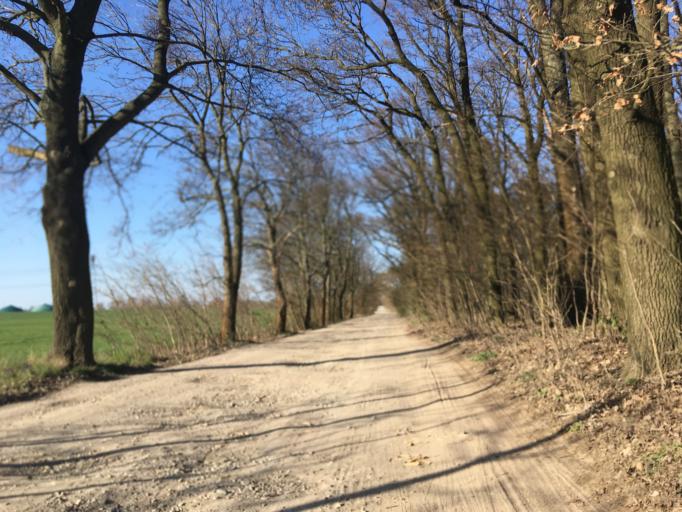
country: DE
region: Brandenburg
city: Ahrensfelde
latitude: 52.6177
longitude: 13.5725
